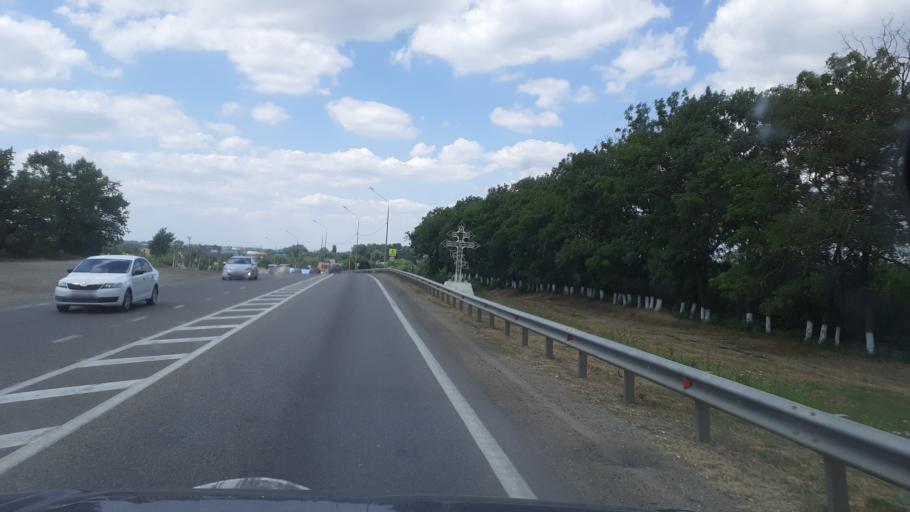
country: RU
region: Krasnodarskiy
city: Il'skiy
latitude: 44.8526
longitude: 38.5948
